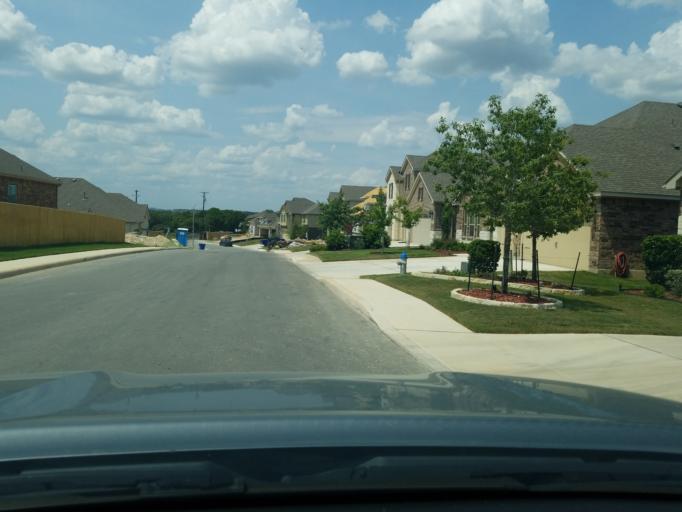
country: US
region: Texas
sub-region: Bexar County
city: Timberwood Park
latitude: 29.6833
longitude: -98.4787
